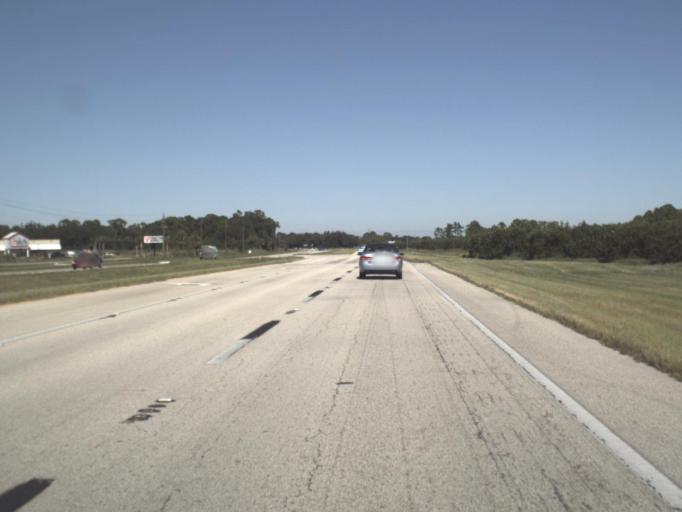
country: US
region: Florida
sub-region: Hendry County
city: LaBelle
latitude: 26.7394
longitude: -81.4685
